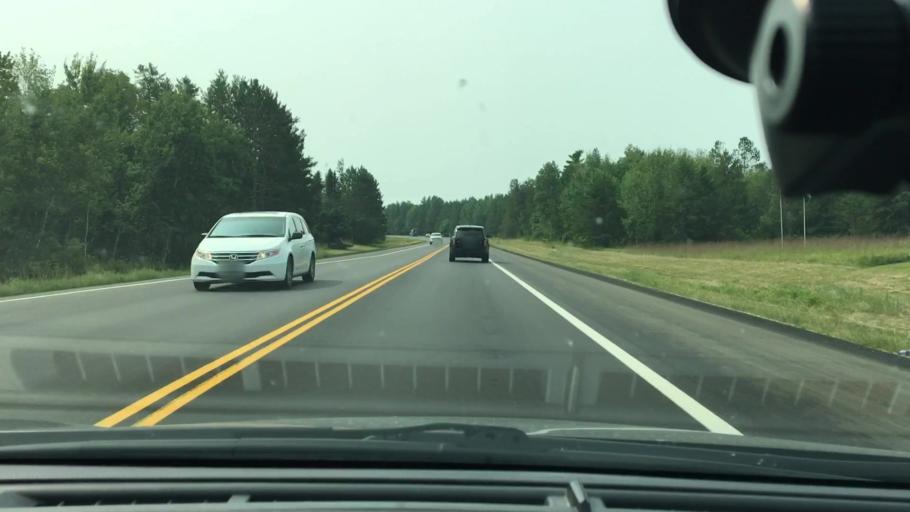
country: US
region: Minnesota
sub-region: Crow Wing County
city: Brainerd
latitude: 46.4269
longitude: -94.1769
